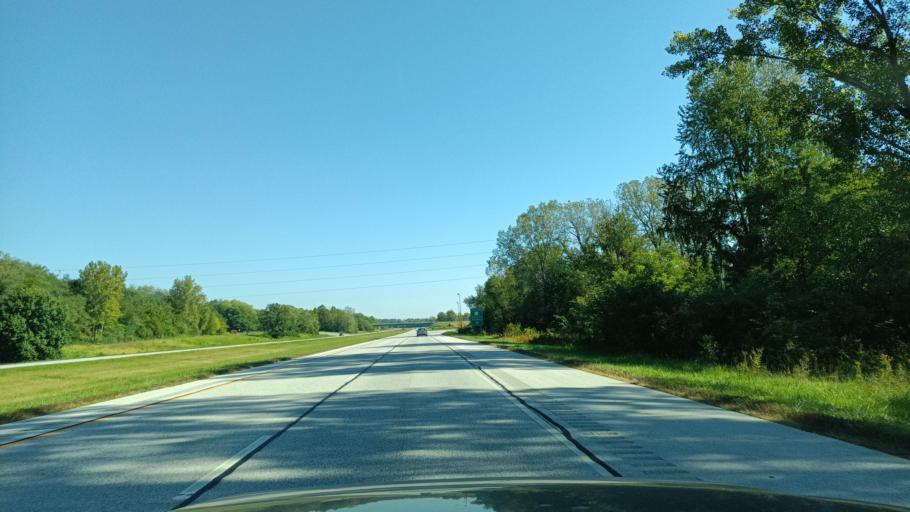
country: US
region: Illinois
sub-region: Adams County
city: Quincy
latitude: 39.8760
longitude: -91.3360
